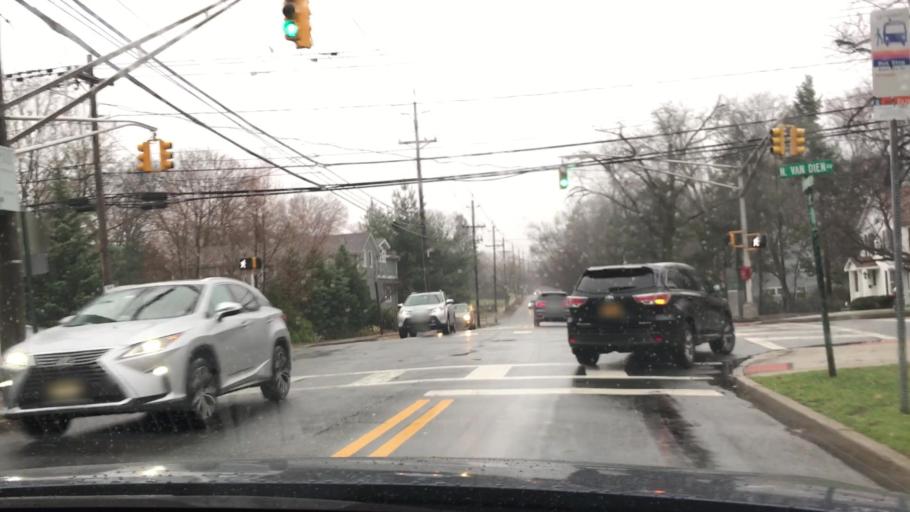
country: US
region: New Jersey
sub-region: Bergen County
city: Ho-Ho-Kus
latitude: 40.9822
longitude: -74.1018
